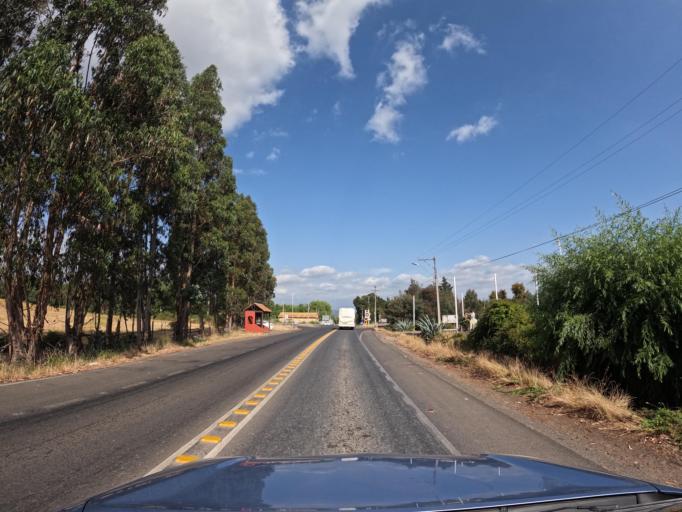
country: CL
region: Maule
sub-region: Provincia de Curico
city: Molina
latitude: -35.2739
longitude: -71.2977
